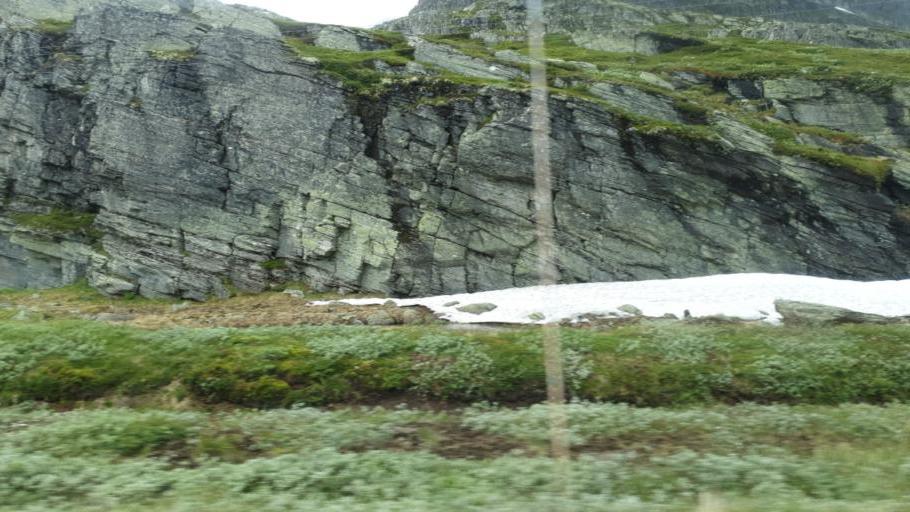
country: NO
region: Oppland
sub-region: Vestre Slidre
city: Slidre
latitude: 61.2907
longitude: 8.8136
